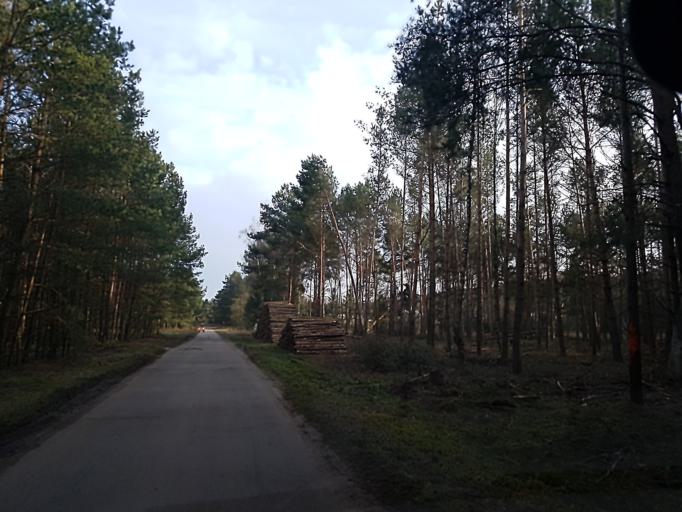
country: DE
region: Brandenburg
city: Wollin
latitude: 52.2708
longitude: 12.4903
